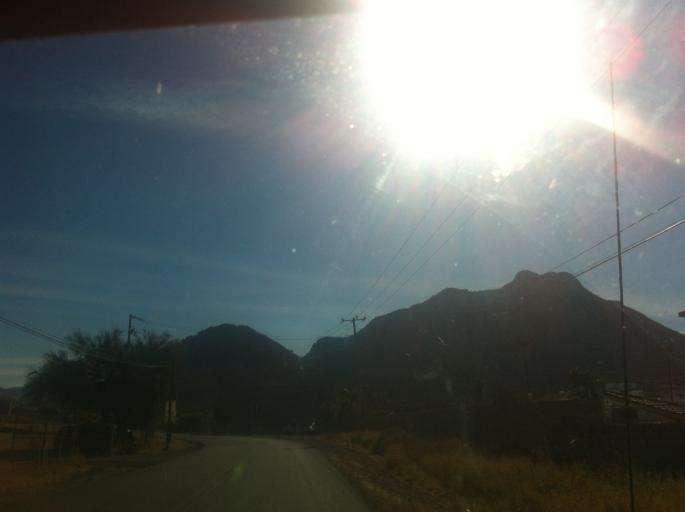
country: MX
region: Sonora
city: Heroica Guaymas
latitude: 27.9286
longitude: -110.9369
